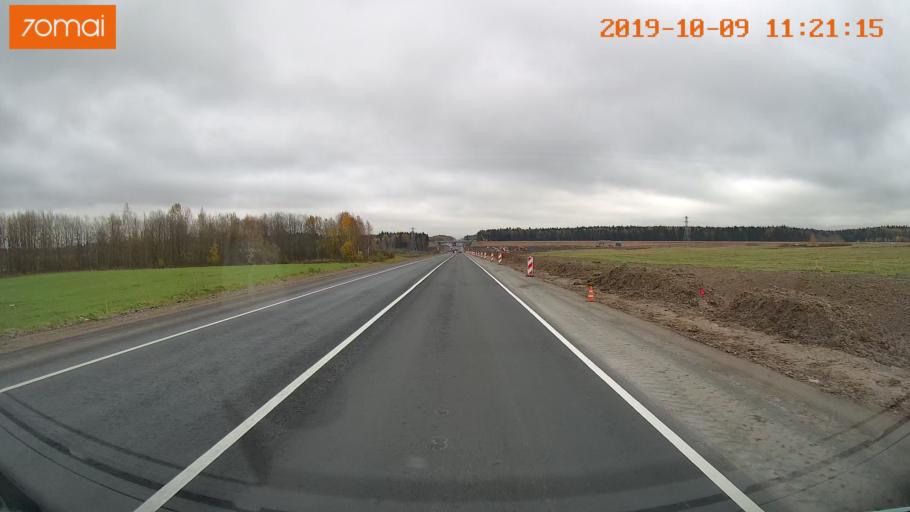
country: RU
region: Vologda
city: Vologda
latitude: 59.1411
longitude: 39.9477
